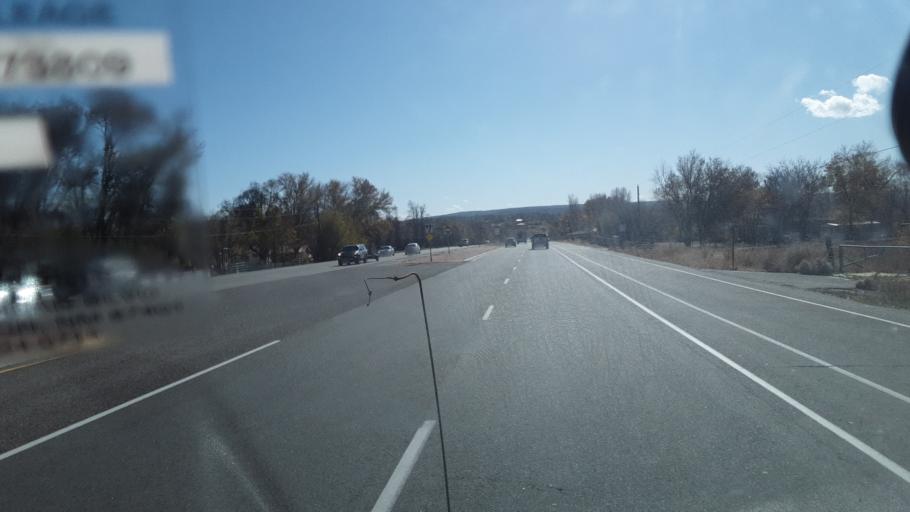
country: US
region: New Mexico
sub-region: Santa Fe County
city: Pojoaque
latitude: 35.9038
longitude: -106.0187
